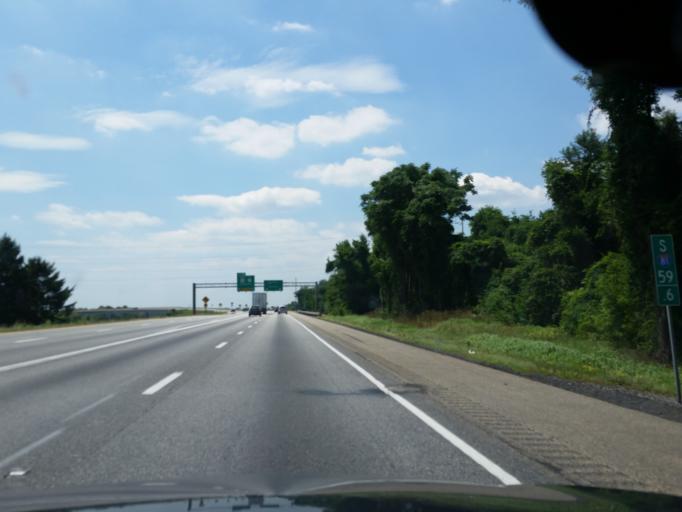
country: US
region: Pennsylvania
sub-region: Cumberland County
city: Enola
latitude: 40.2758
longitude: -76.9950
